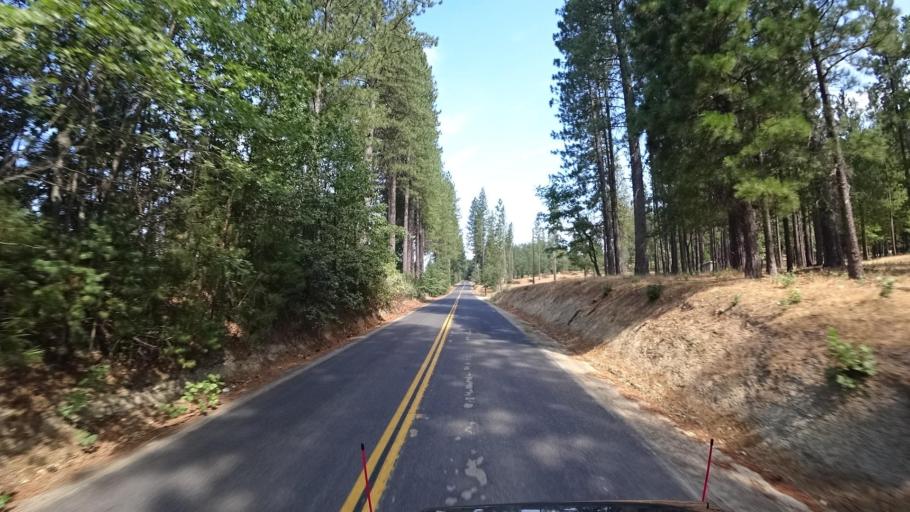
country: US
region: California
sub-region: Tuolumne County
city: Tuolumne City
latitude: 37.7505
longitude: -120.1362
